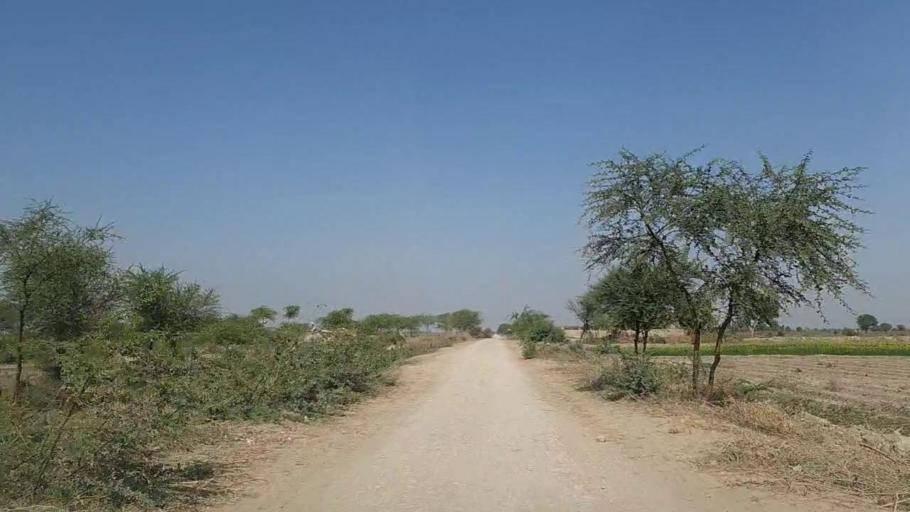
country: PK
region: Sindh
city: Samaro
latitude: 25.1966
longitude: 69.4041
